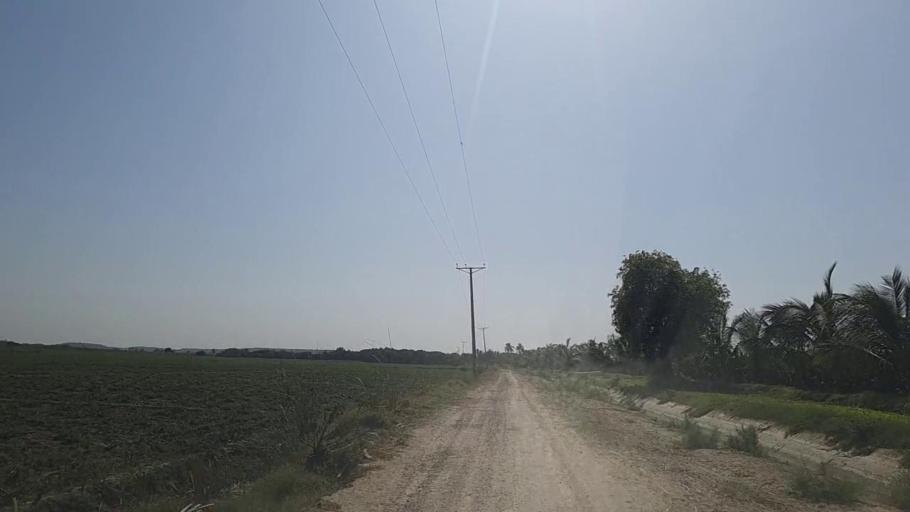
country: PK
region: Sindh
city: Thatta
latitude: 24.6323
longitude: 67.8815
